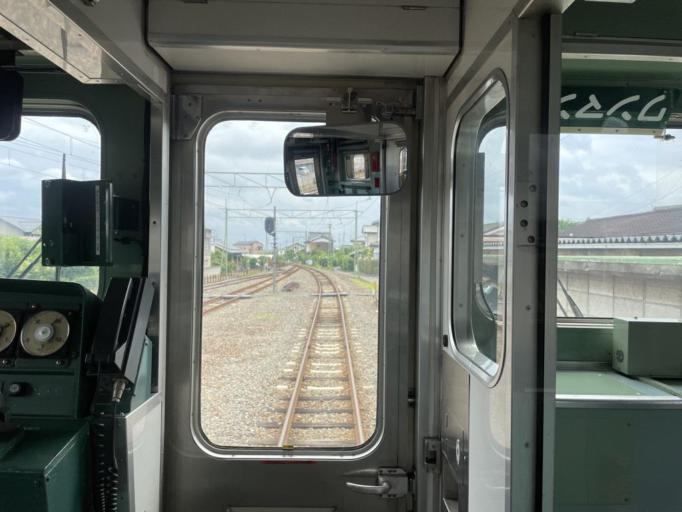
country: JP
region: Gunma
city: Yoshii
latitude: 36.2561
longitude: 138.9847
